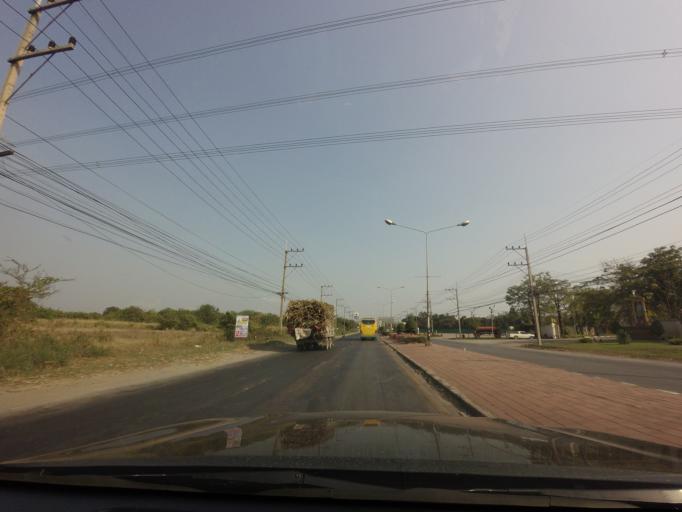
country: TH
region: Kanchanaburi
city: Tha Maka
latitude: 13.8811
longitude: 99.8059
